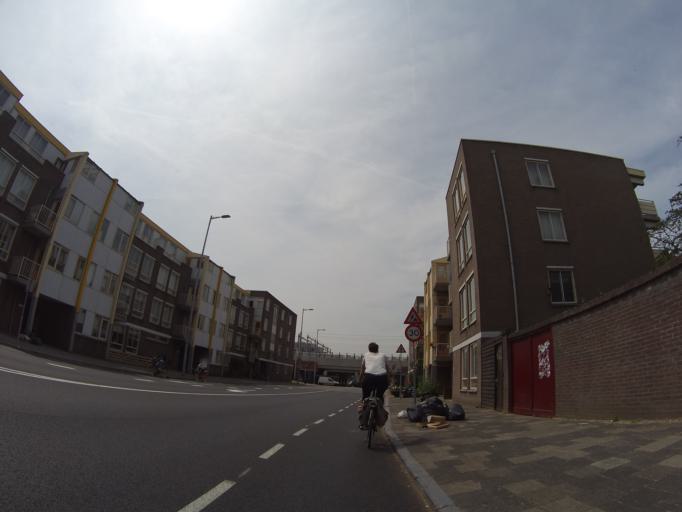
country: NL
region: Utrecht
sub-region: Gemeente Utrecht
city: Utrecht
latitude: 52.0802
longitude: 5.1216
